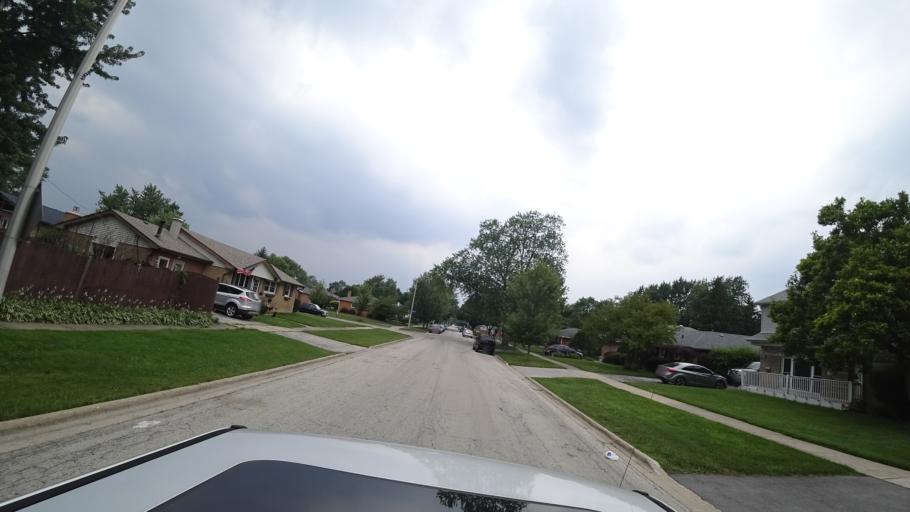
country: US
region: Illinois
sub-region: Cook County
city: Chicago Ridge
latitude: 41.6923
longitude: -87.7672
